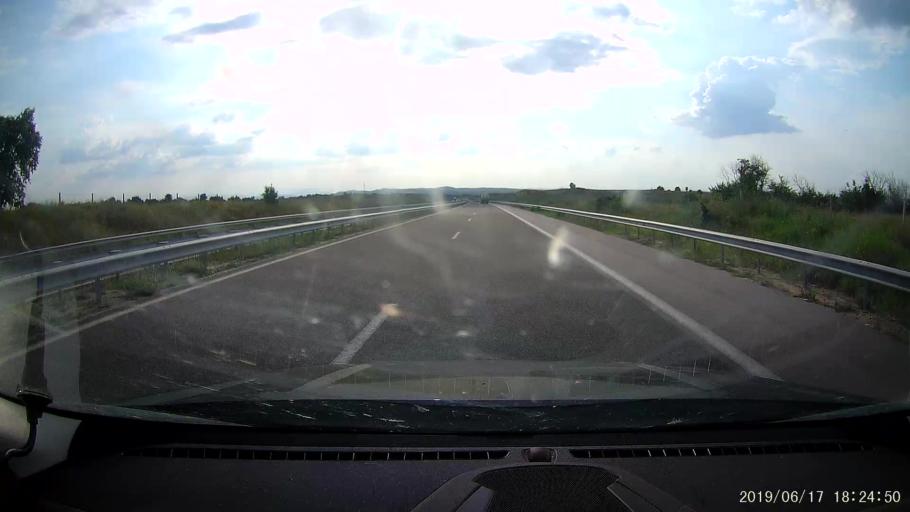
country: BG
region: Khaskovo
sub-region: Obshtina Dimitrovgrad
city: Dimitrovgrad
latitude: 41.9878
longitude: 25.6797
